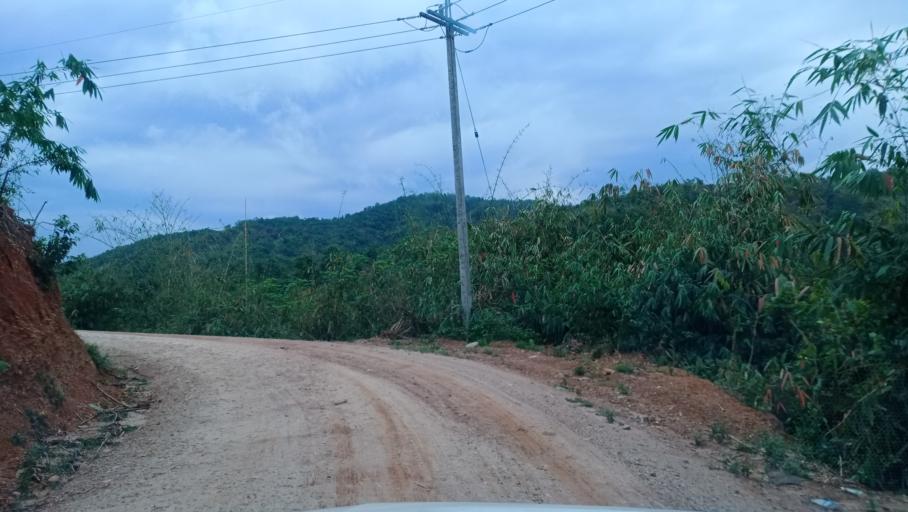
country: LA
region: Phongsali
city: Khoa
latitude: 21.1941
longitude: 102.6945
